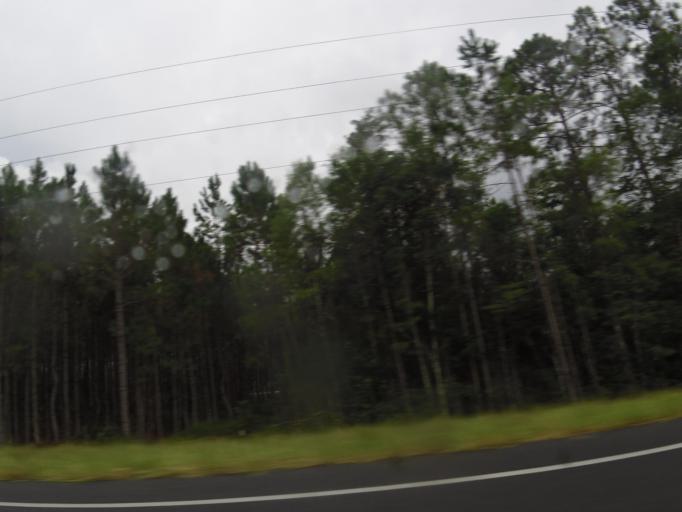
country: US
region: Florida
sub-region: Baker County
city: Macclenny
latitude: 30.3694
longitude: -82.1490
